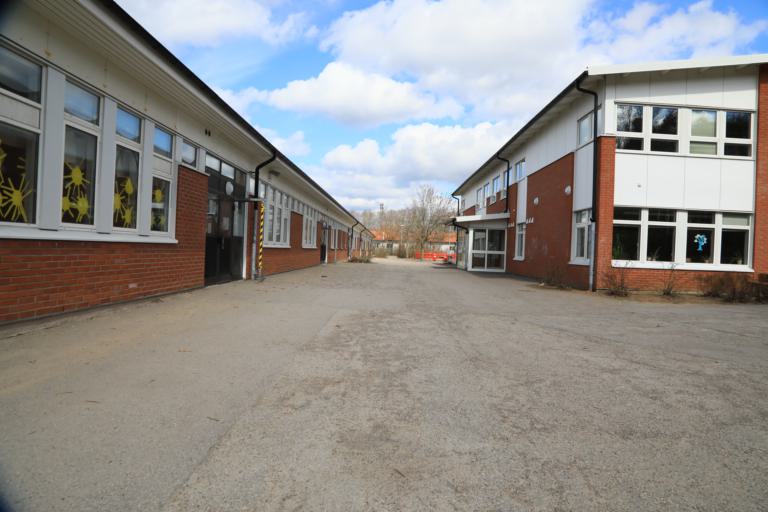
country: SE
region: Halland
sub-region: Varbergs Kommun
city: Varberg
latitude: 57.0955
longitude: 12.2663
